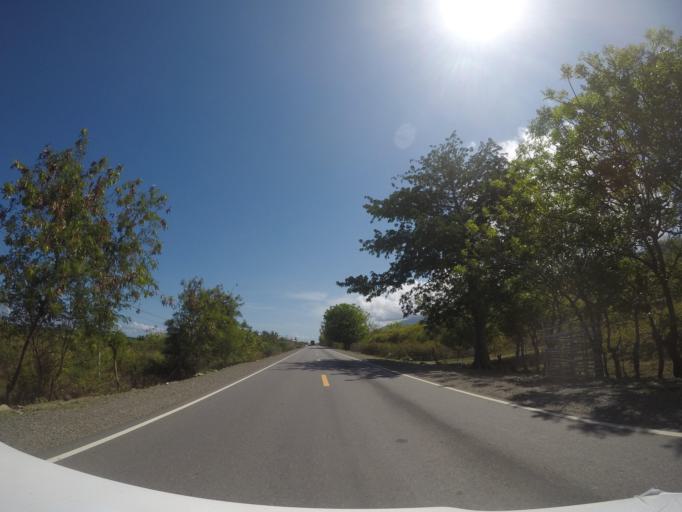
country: ID
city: Metinaro
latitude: -8.5247
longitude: 125.7643
